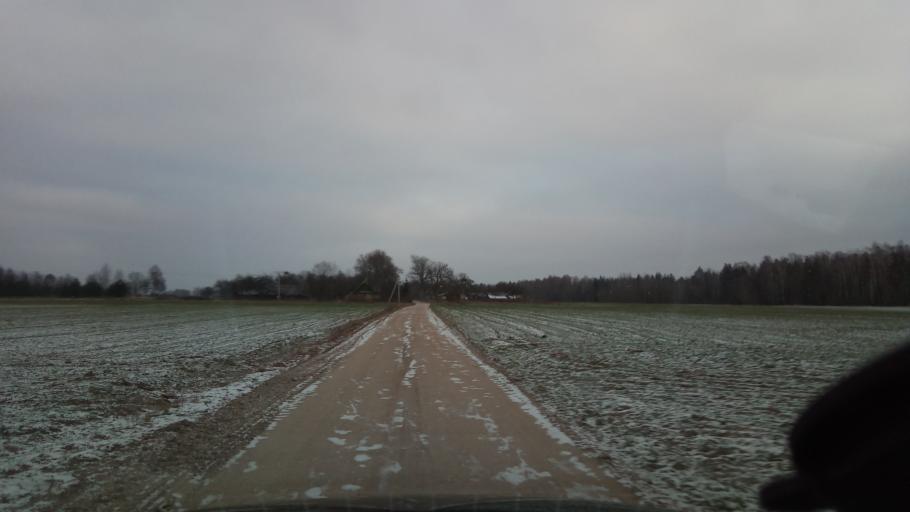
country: LT
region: Alytaus apskritis
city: Varena
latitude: 54.1247
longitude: 24.7055
